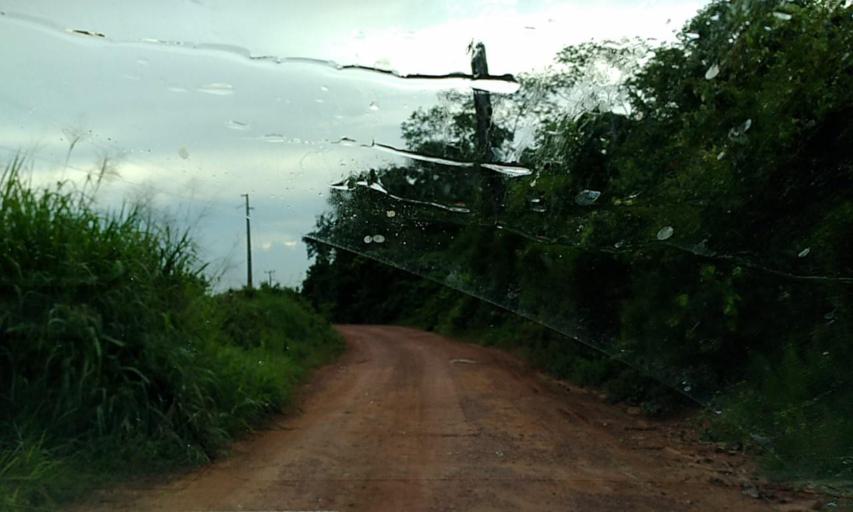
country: BR
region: Para
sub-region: Senador Jose Porfirio
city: Senador Jose Porfirio
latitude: -2.5534
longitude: -51.8685
